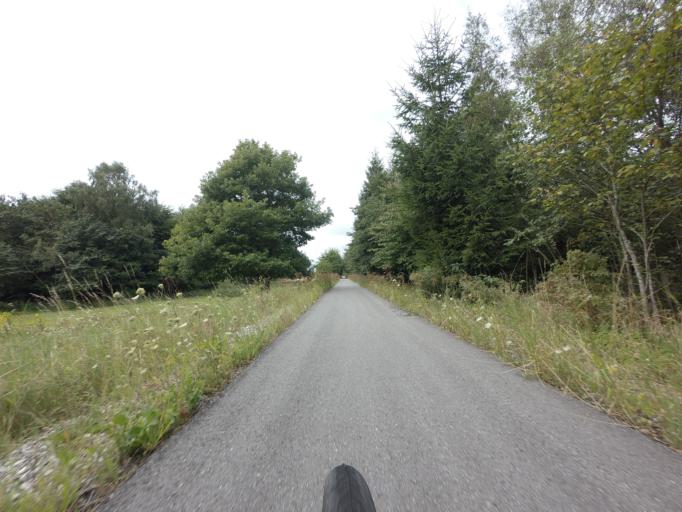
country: DK
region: Central Jutland
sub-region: Syddjurs Kommune
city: Ryomgard
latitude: 56.3861
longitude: 10.4411
